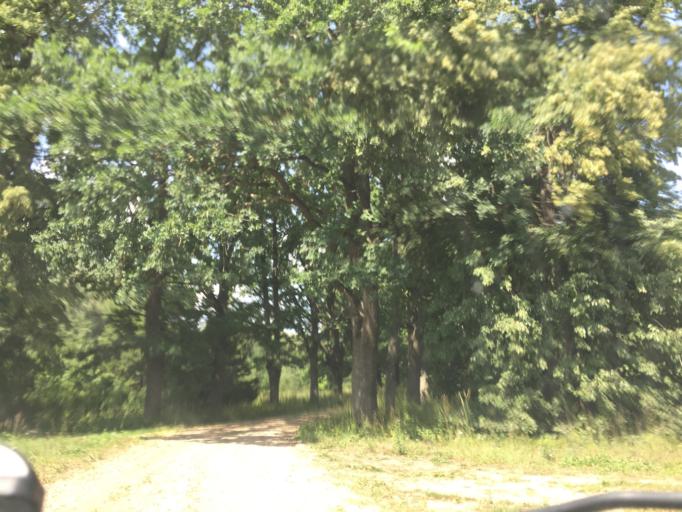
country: LT
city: Zagare
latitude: 56.3853
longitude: 23.2053
